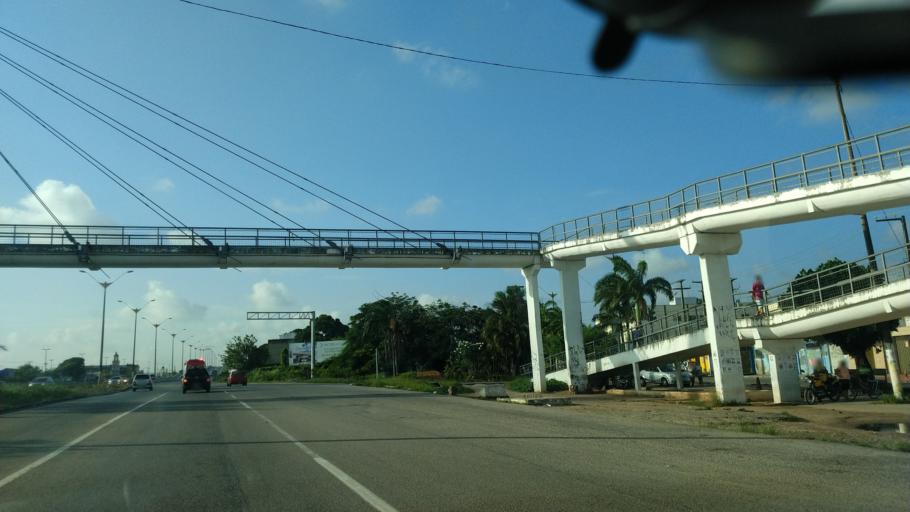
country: BR
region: Rio Grande do Norte
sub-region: Parnamirim
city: Parnamirim
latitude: -5.9276
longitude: -35.2646
